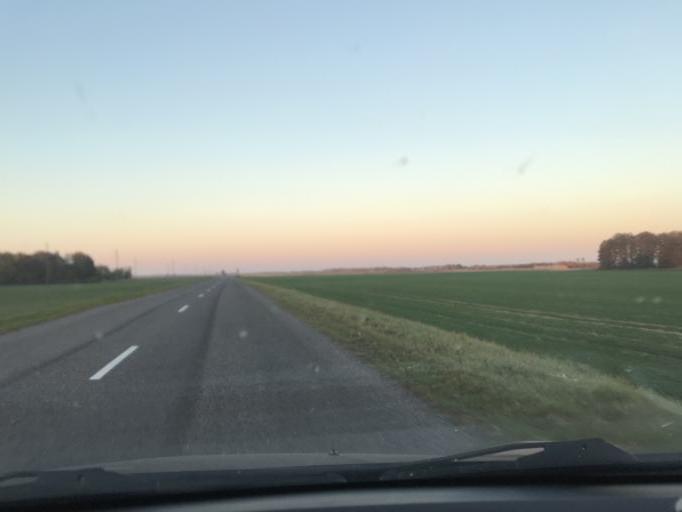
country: BY
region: Gomel
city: Loyew
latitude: 52.0862
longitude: 30.5503
